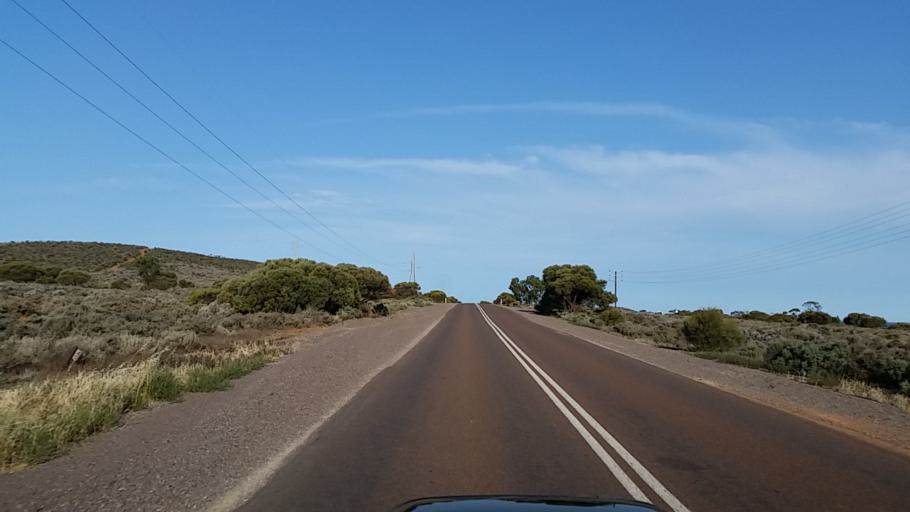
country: AU
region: South Australia
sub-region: Whyalla
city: Whyalla
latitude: -33.0078
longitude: 137.5340
